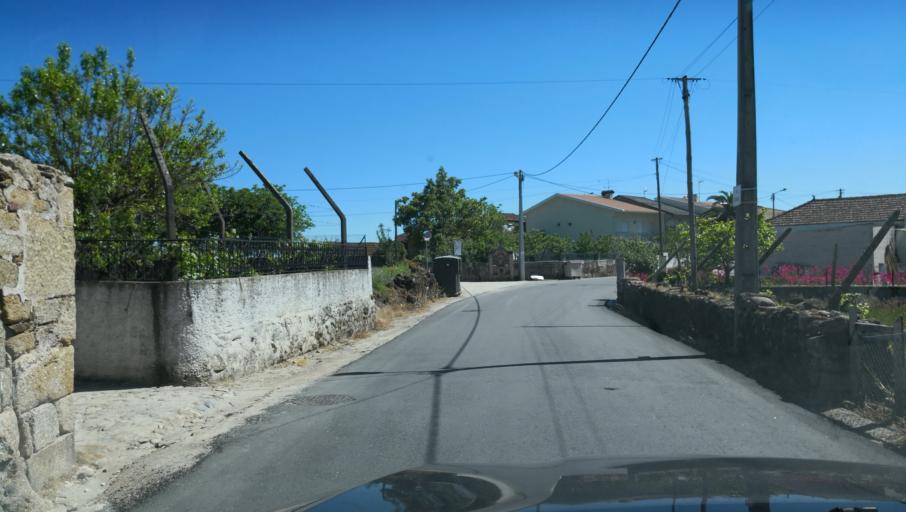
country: PT
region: Vila Real
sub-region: Vila Real
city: Vila Real
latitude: 41.2832
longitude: -7.6835
